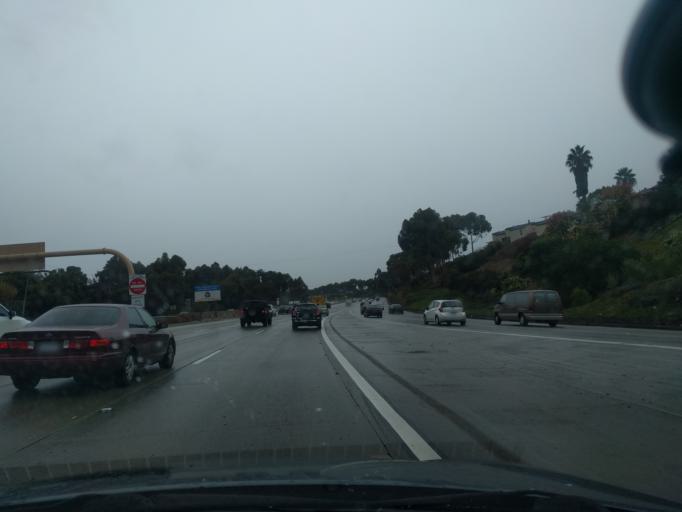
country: US
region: California
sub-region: San Diego County
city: San Diego
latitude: 32.7413
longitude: -117.1125
